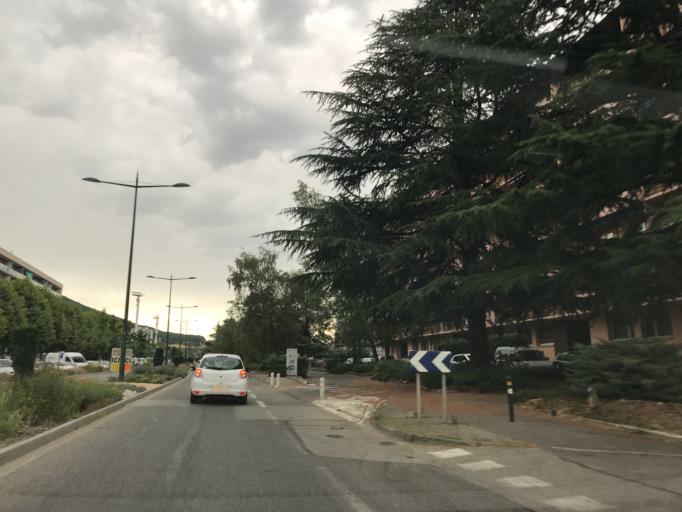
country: FR
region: Rhone-Alpes
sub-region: Departement de la Savoie
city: Aix-les-Bains
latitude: 45.6993
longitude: 5.9085
